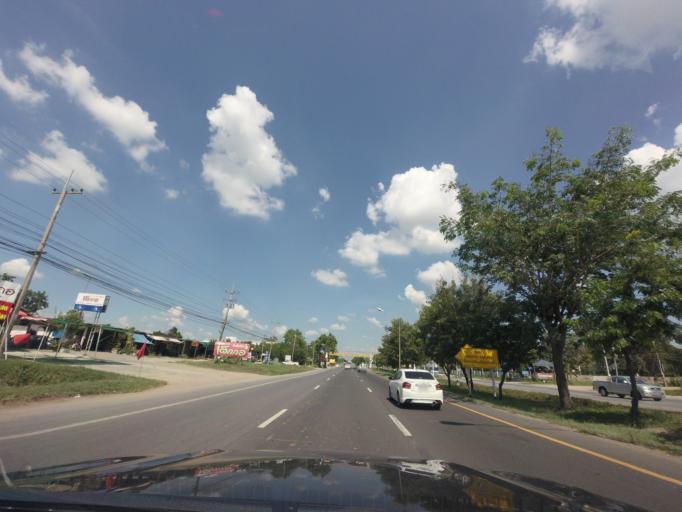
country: TH
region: Nakhon Ratchasima
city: Chaloem Phra Kiat
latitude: 15.0606
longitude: 102.1737
